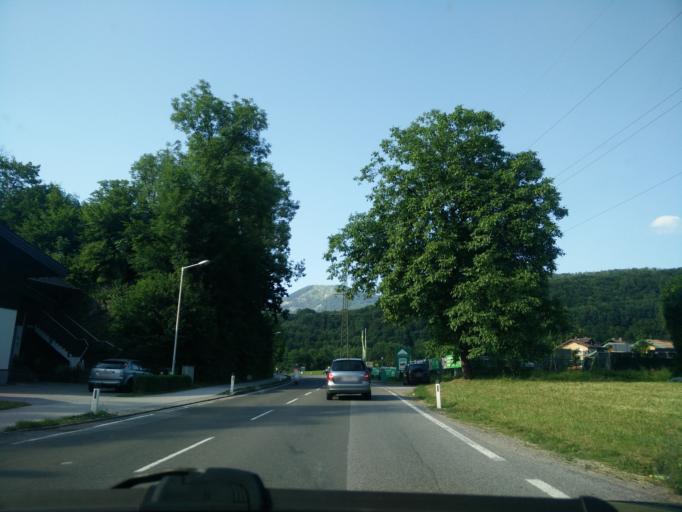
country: AT
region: Salzburg
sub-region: Politischer Bezirk Salzburg-Umgebung
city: Elsbethen
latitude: 47.7657
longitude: 13.0883
